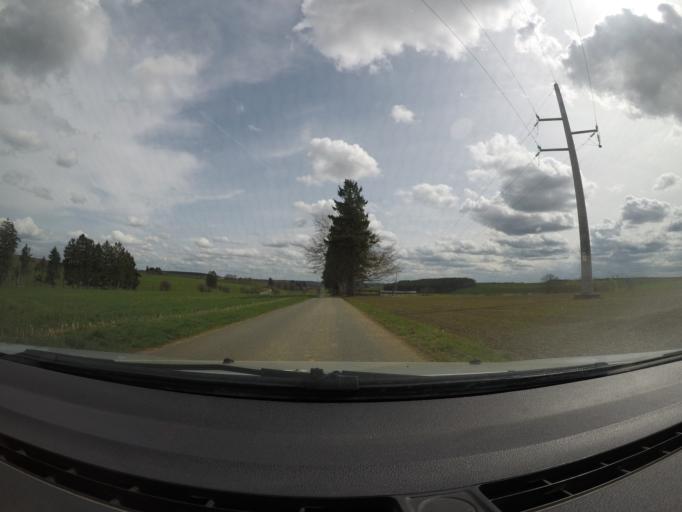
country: BE
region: Wallonia
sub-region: Province du Luxembourg
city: Neufchateau
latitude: 49.8247
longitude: 5.4588
